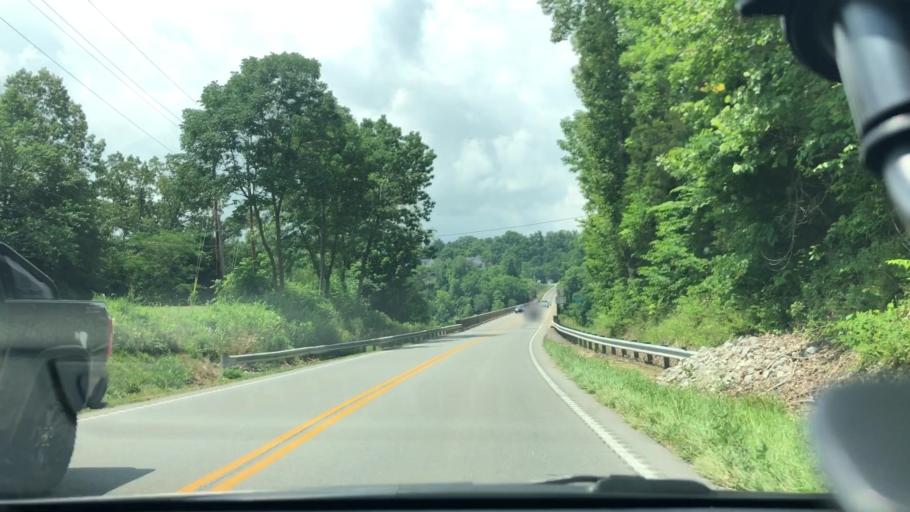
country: US
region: Kentucky
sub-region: Pulaski County
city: Somerset
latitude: 37.0536
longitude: -84.6771
